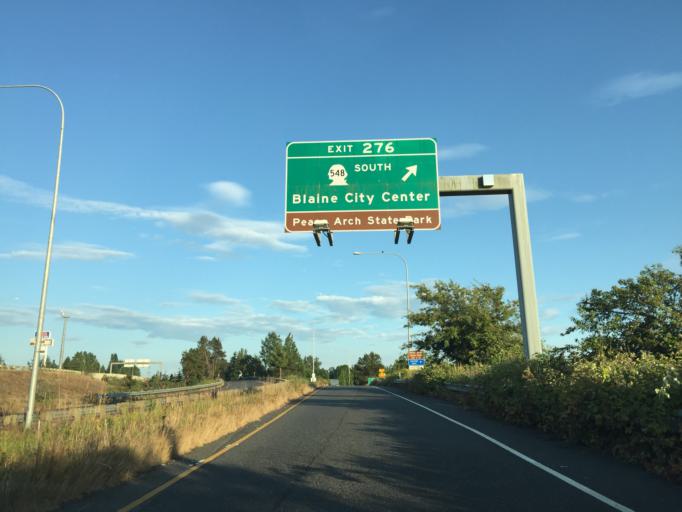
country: US
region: Washington
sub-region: Whatcom County
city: Blaine
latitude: 48.9989
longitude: -122.7542
